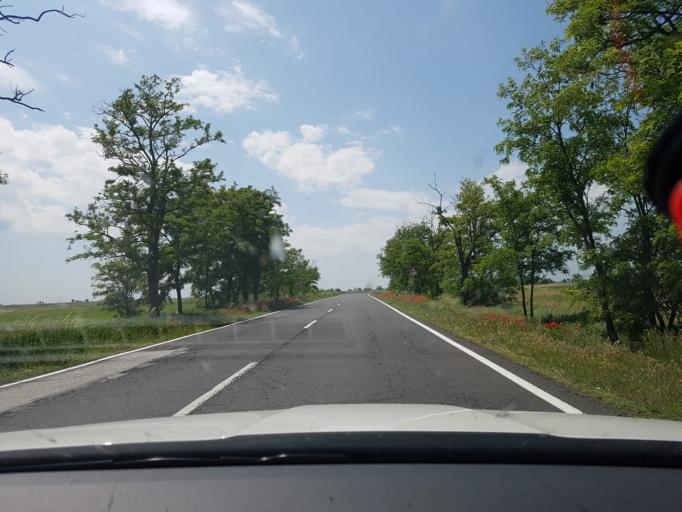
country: HU
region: Hajdu-Bihar
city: Egyek
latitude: 47.5541
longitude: 20.9635
